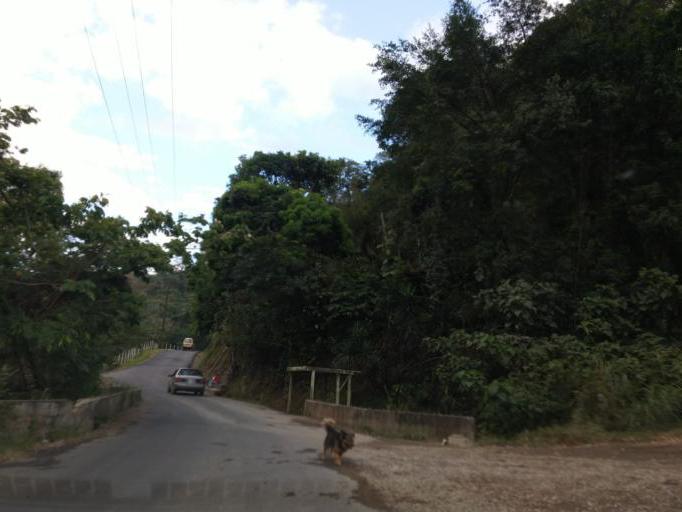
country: CR
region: San Jose
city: San Ignacio
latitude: 9.8105
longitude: -84.1833
